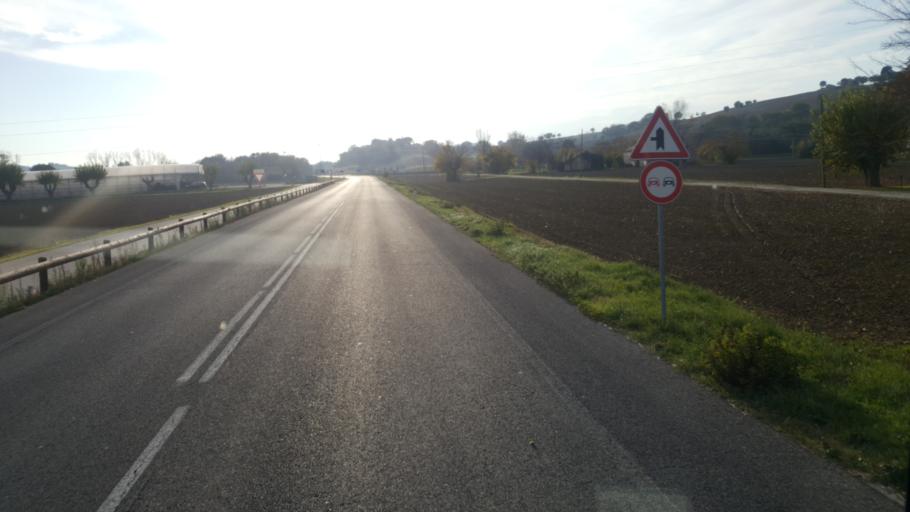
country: IT
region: The Marches
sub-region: Provincia di Ancona
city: Casine
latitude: 43.6449
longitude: 13.1432
